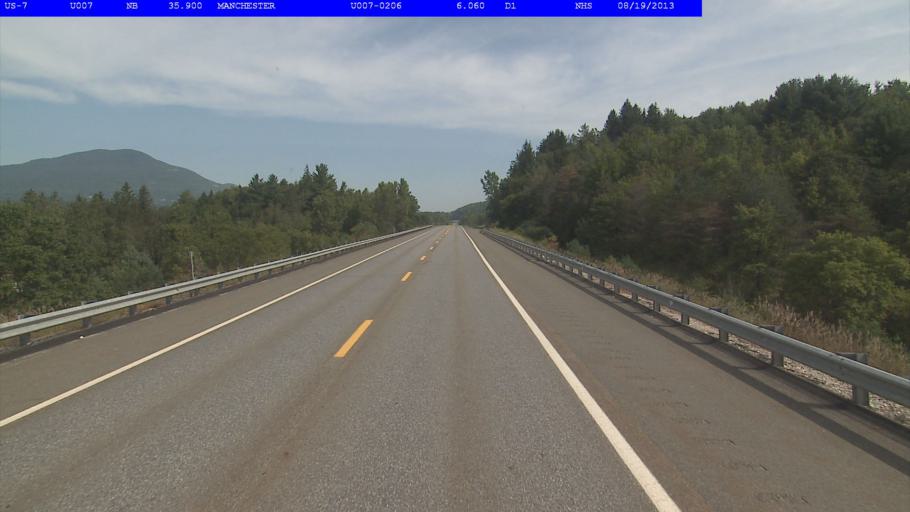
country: US
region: Vermont
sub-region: Bennington County
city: Manchester Center
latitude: 43.1897
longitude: -73.0145
